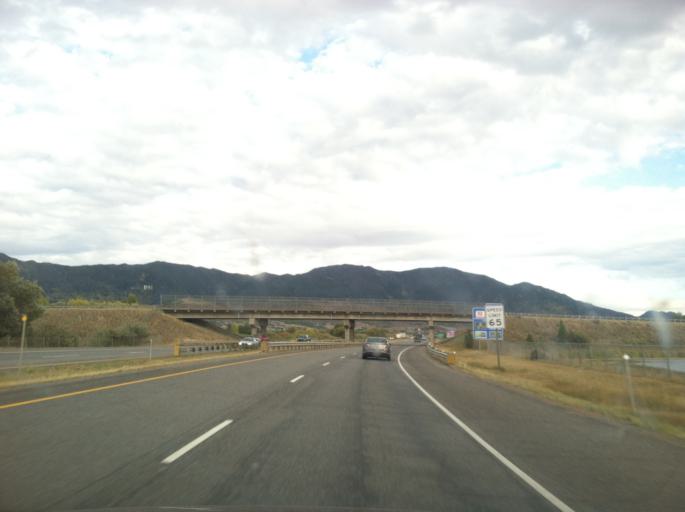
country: US
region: Montana
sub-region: Silver Bow County
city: Butte
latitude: 45.9920
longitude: -112.5308
